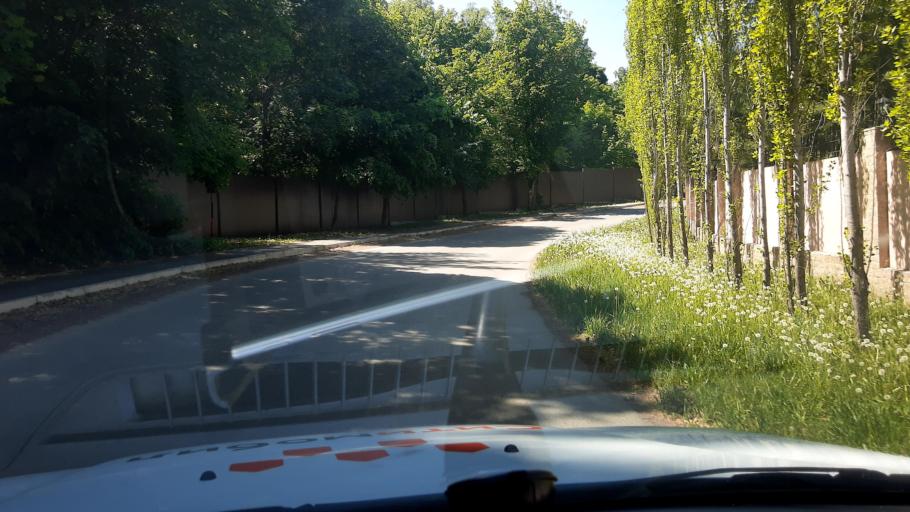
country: RU
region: Bashkortostan
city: Ufa
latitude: 54.6008
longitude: 55.9607
